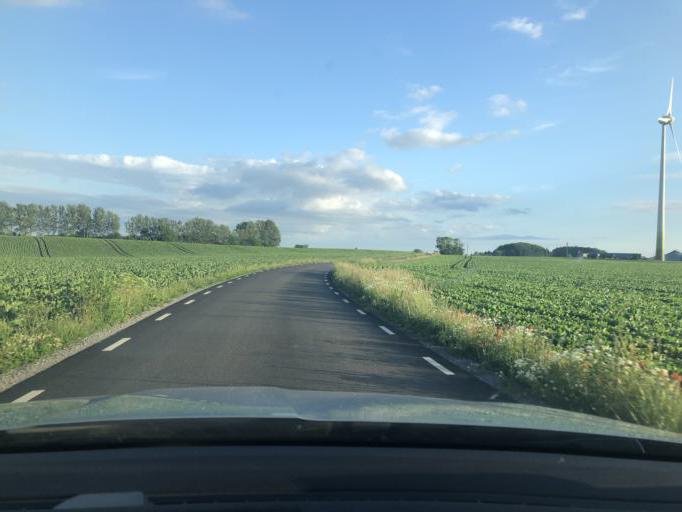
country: SE
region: Skane
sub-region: Simrishamns Kommun
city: Simrishamn
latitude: 55.4730
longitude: 14.1935
